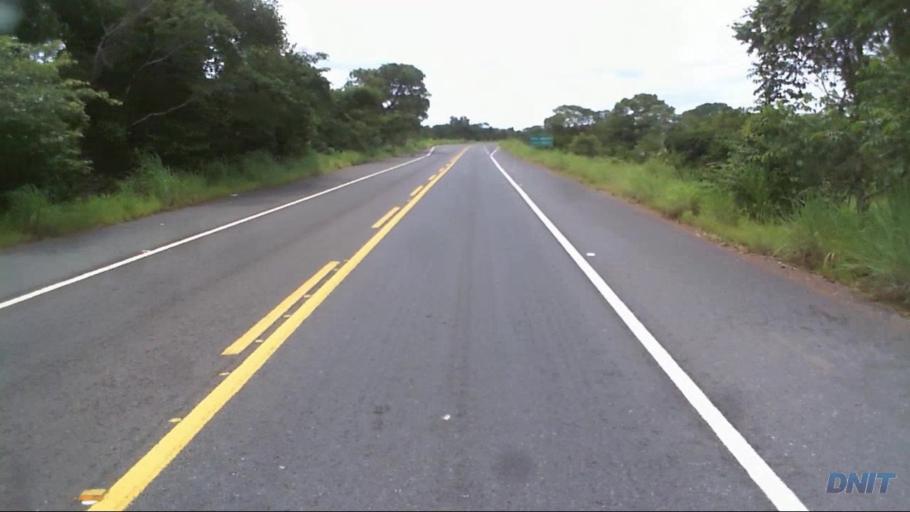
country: BR
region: Goias
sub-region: Sao Miguel Do Araguaia
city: Sao Miguel do Araguaia
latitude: -13.2345
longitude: -50.5604
